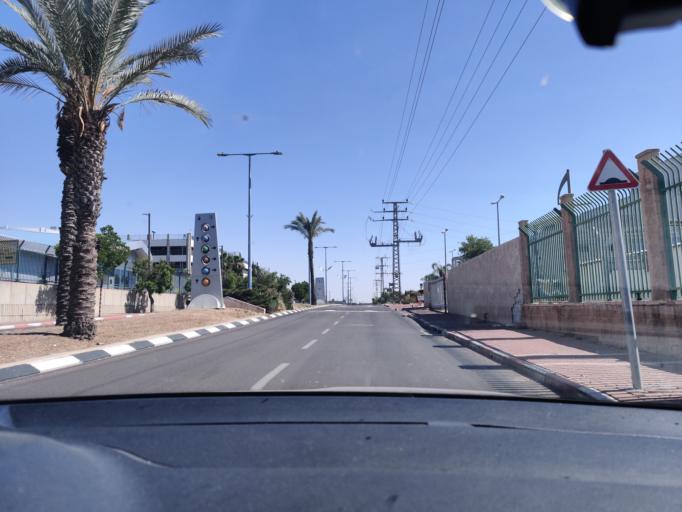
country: IL
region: Southern District
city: Qiryat Gat
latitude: 31.5960
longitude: 34.7862
